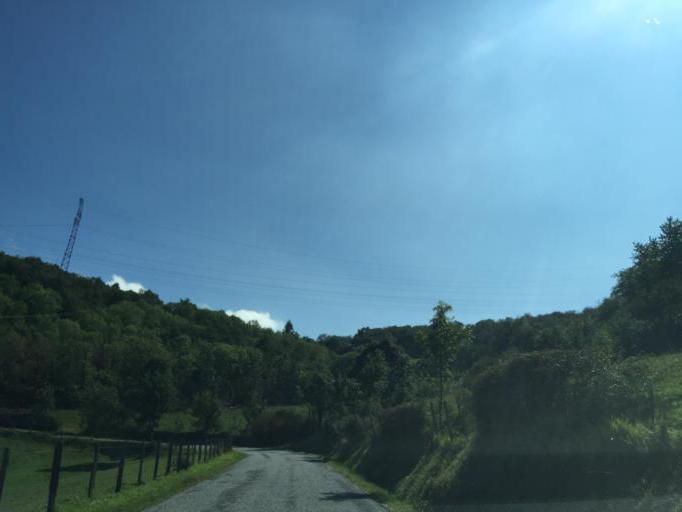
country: FR
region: Rhone-Alpes
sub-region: Departement de la Loire
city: Saint-Chamond
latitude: 45.4587
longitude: 4.5241
